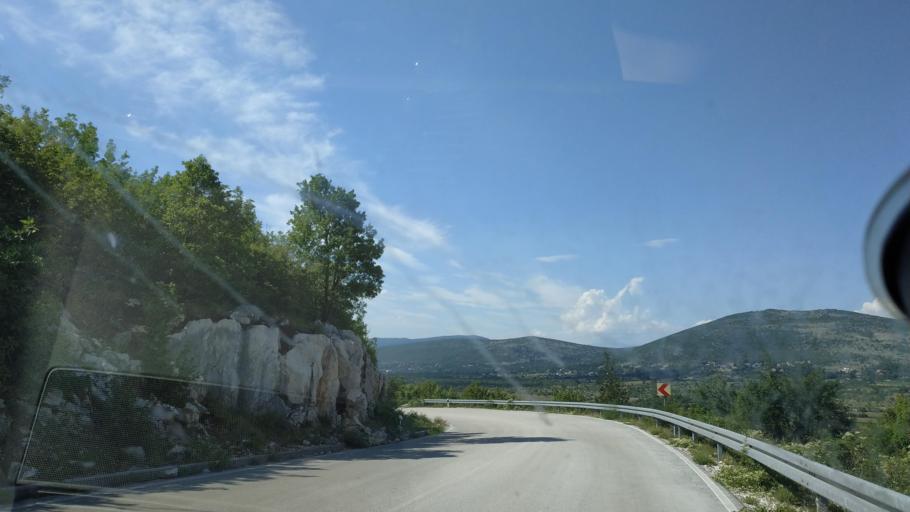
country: HR
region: Splitsko-Dalmatinska
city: Greda
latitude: 43.5831
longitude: 16.6540
